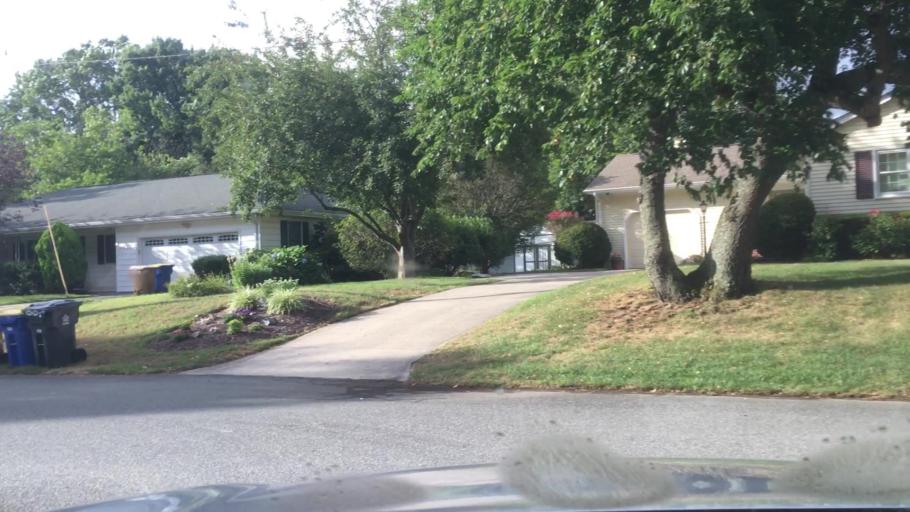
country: US
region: Delaware
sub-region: Sussex County
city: Milford
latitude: 38.9072
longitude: -75.4391
